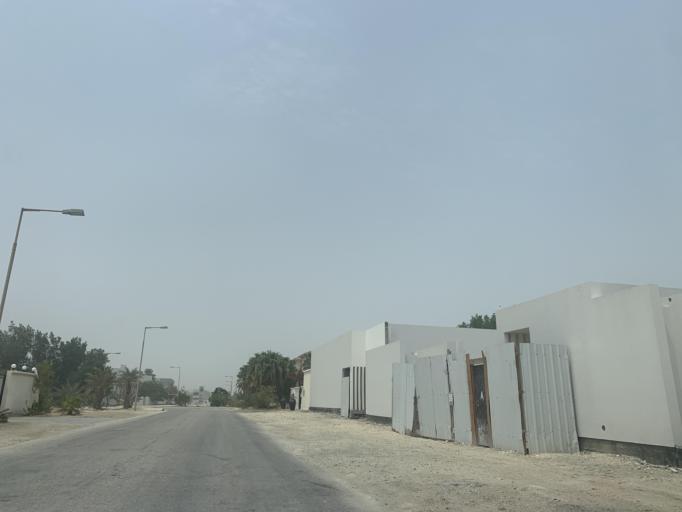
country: BH
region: Central Governorate
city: Madinat Hamad
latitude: 26.1629
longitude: 50.4768
